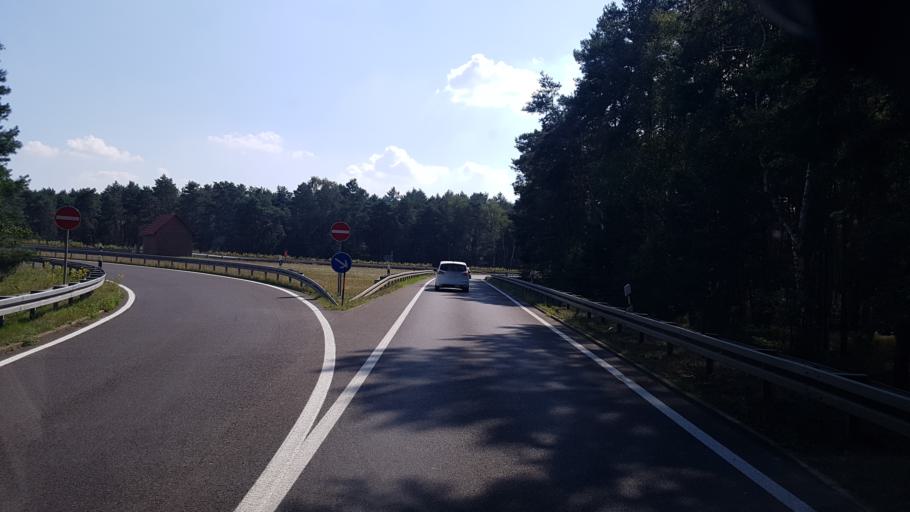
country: DE
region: Brandenburg
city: Heinersbruck
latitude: 51.7130
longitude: 14.4617
